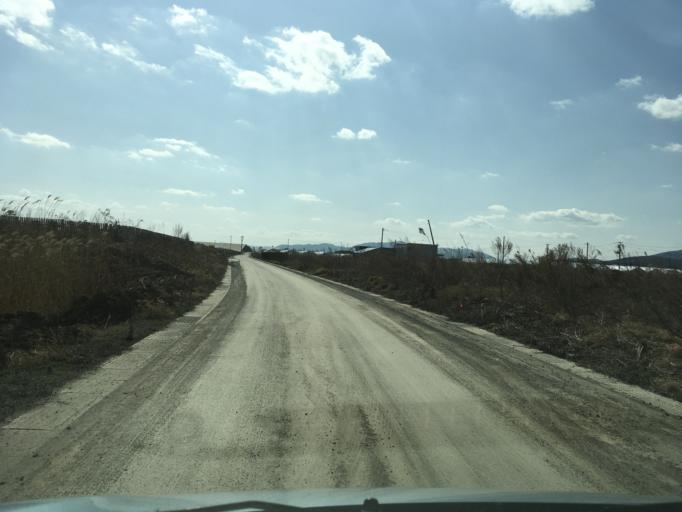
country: JP
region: Iwate
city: Ofunato
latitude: 38.8277
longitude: 141.5929
